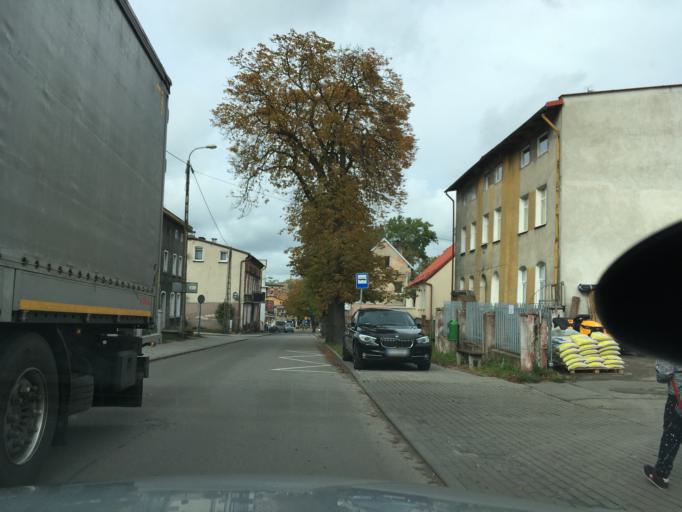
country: PL
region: Pomeranian Voivodeship
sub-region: Powiat koscierski
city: Koscierzyna
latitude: 54.1202
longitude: 17.9820
